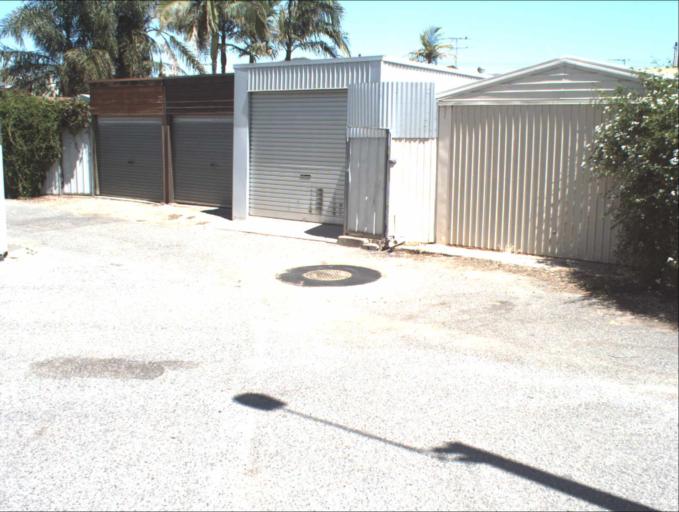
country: AU
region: South Australia
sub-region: Port Adelaide Enfield
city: Alberton
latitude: -34.8548
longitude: 138.5065
